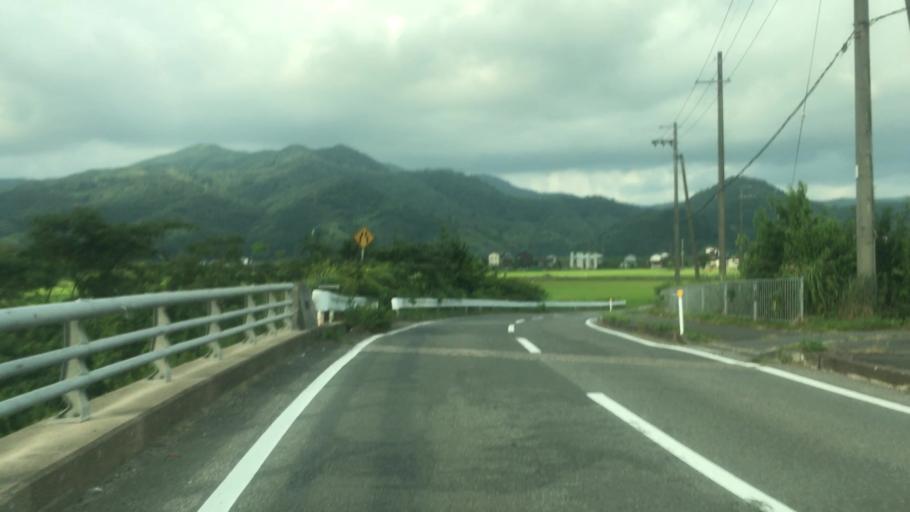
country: JP
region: Hyogo
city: Toyooka
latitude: 35.5645
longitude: 134.8055
